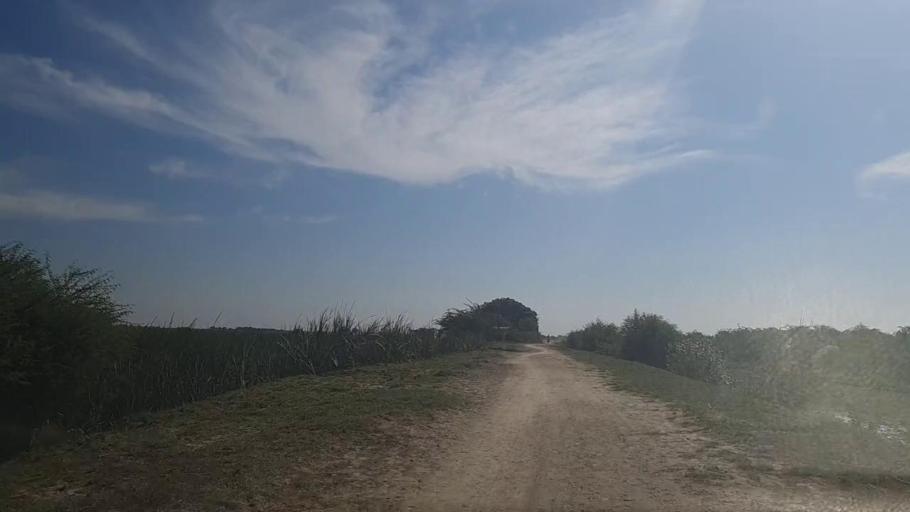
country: PK
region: Sindh
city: Mirpur Batoro
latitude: 24.6604
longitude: 68.1935
